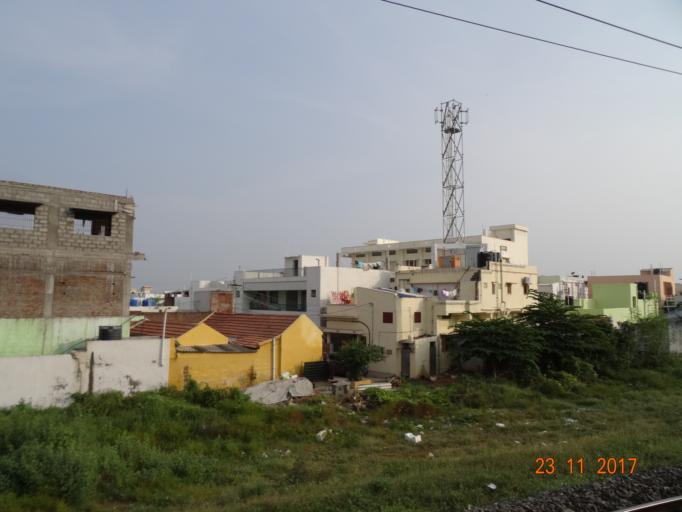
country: IN
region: Tamil Nadu
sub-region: Tiruppur
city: Tiruppur
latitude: 11.1201
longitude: 77.3659
